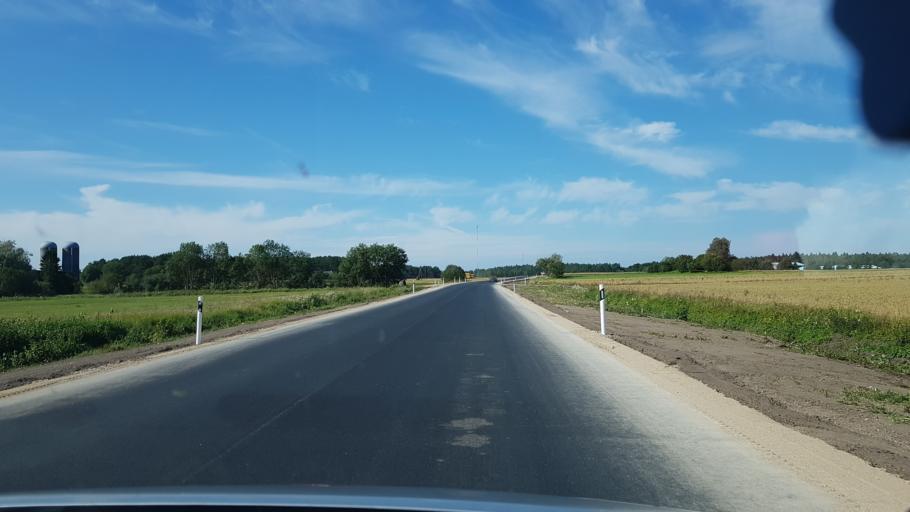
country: EE
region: Laeaene
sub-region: Ridala Parish
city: Uuemoisa
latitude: 59.0038
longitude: 23.7488
